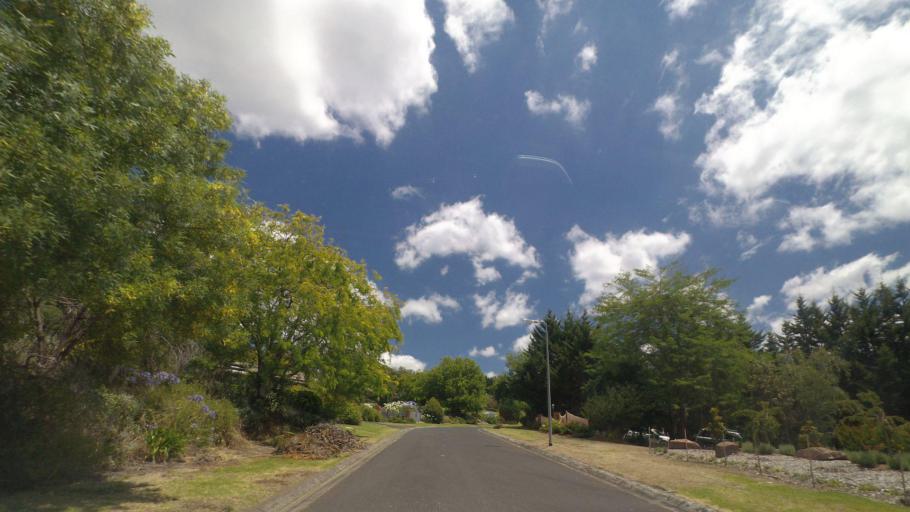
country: AU
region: Victoria
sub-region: Yarra Ranges
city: Chirnside Park
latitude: -37.7351
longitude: 145.2767
